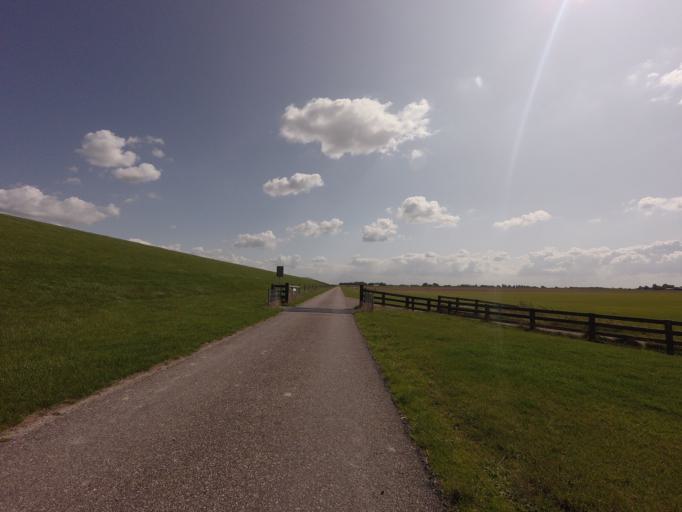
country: NL
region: Friesland
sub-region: Gemeente Ferwerderadiel
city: Hallum
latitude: 53.3217
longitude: 5.7450
